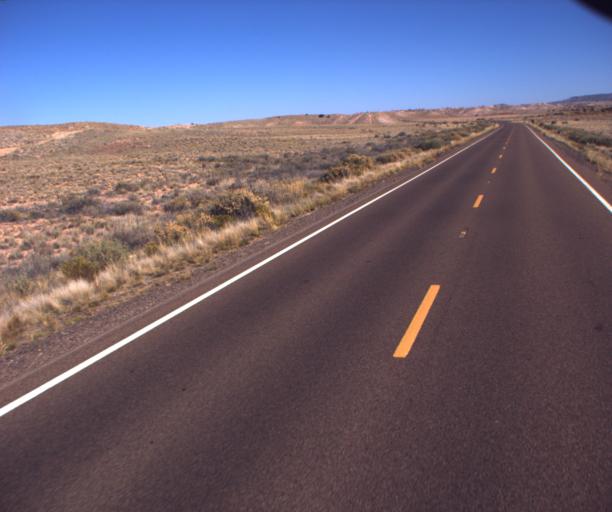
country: US
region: Arizona
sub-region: Navajo County
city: Joseph City
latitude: 35.1678
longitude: -110.4496
